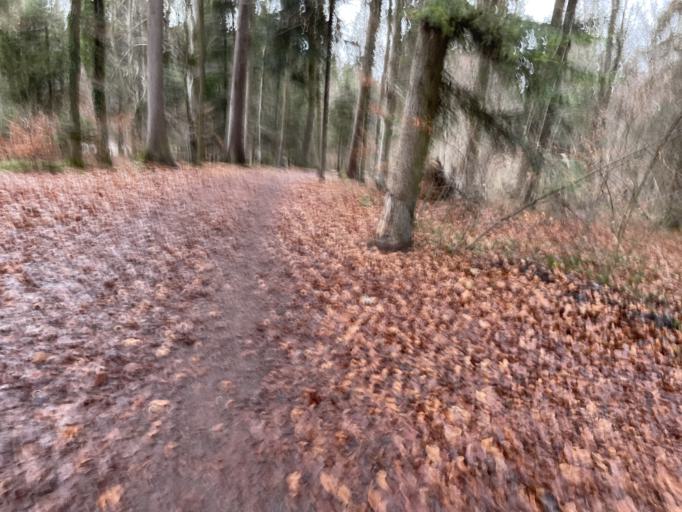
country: CH
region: Bern
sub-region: Thun District
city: Uttigen
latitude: 46.8076
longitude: 7.5702
